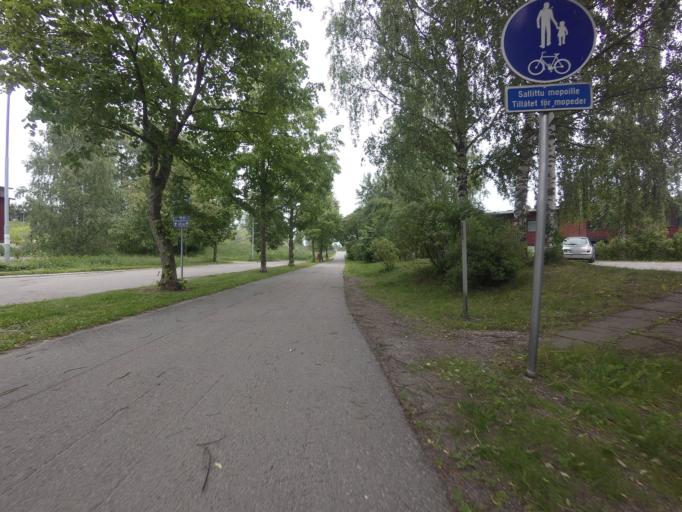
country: FI
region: Uusimaa
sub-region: Helsinki
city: Koukkuniemi
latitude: 60.1748
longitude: 24.7527
